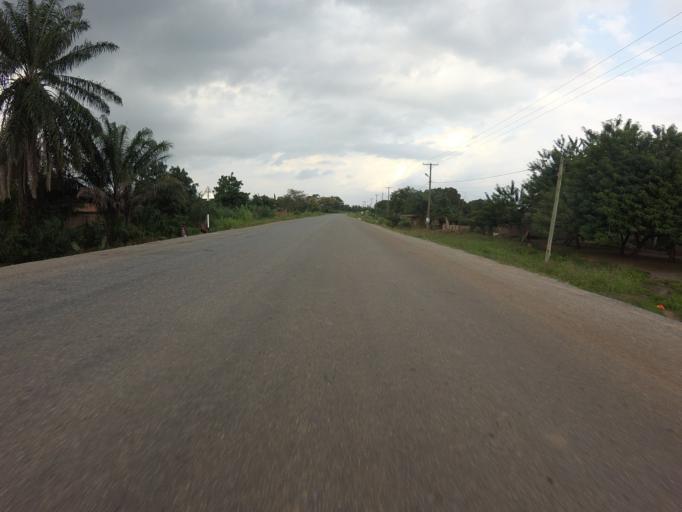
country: GH
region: Volta
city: Ho
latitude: 6.4269
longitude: 0.5133
